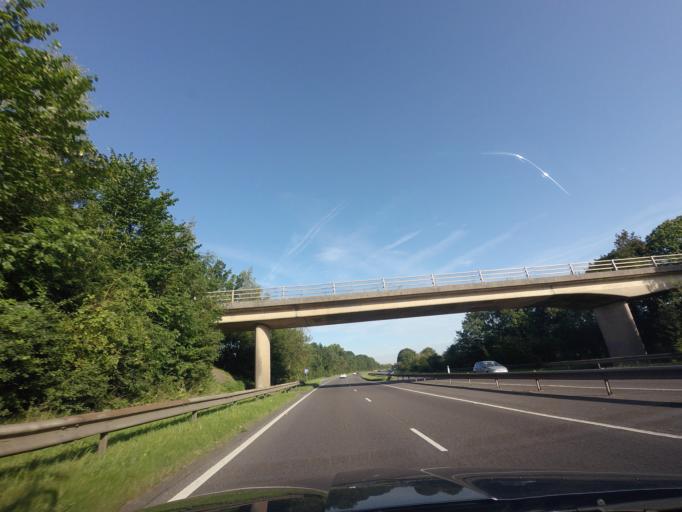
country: GB
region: England
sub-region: Derbyshire
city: Chesterfield
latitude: 53.2134
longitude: -1.3918
